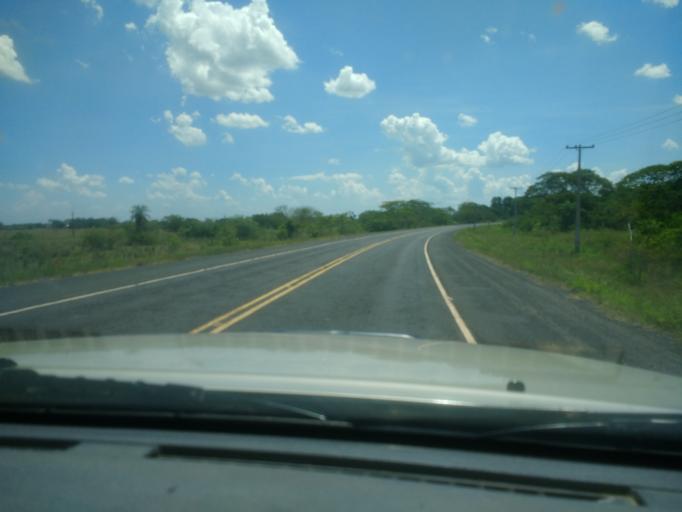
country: PY
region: San Pedro
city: Itacurubi del Rosario
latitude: -24.5261
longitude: -56.8366
